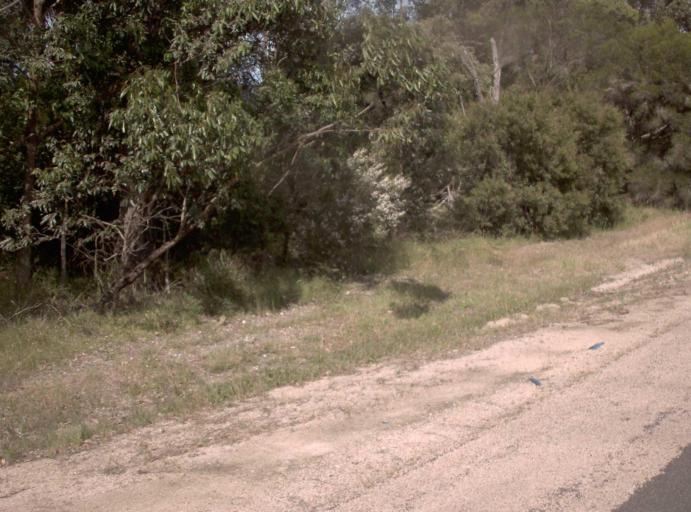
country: AU
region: Victoria
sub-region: East Gippsland
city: Lakes Entrance
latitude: -37.8341
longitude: 147.9100
